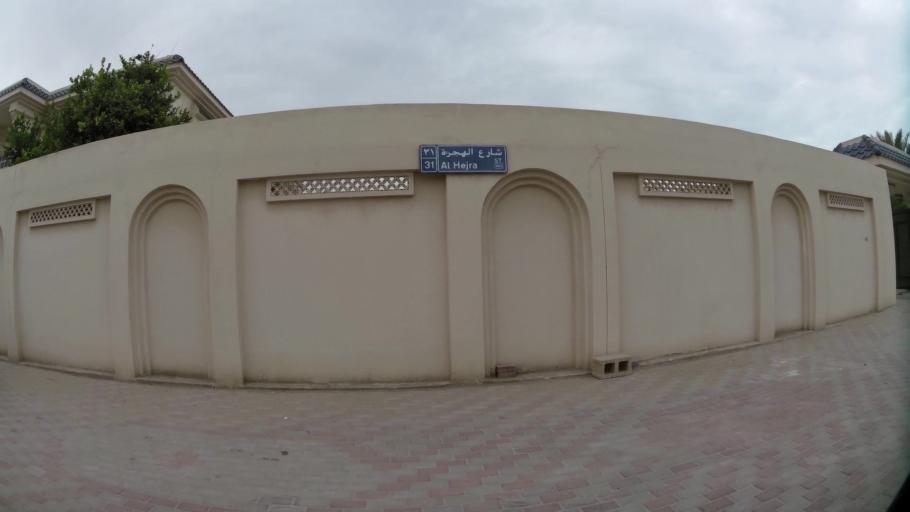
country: QA
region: Baladiyat ar Rayyan
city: Ar Rayyan
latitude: 25.3420
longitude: 51.4617
